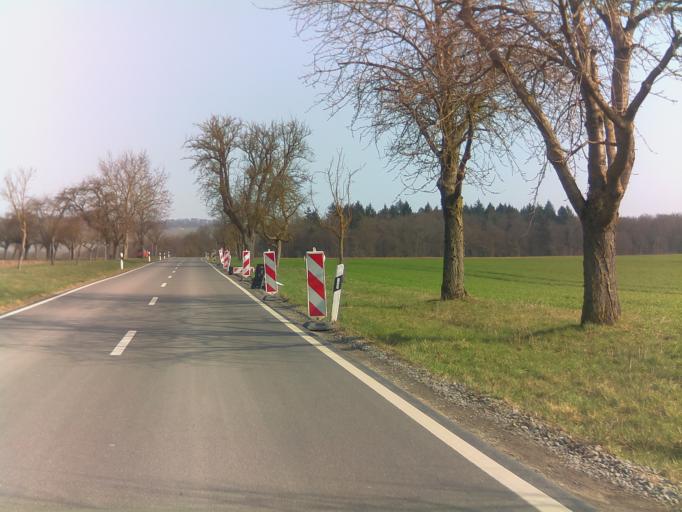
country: DE
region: Baden-Wuerttemberg
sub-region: Regierungsbezirk Stuttgart
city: Sersheim
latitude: 48.9694
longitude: 9.0177
